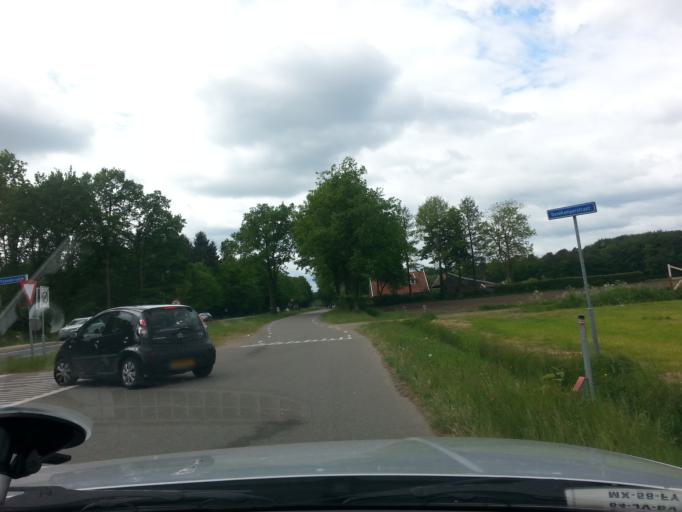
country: NL
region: Overijssel
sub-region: Gemeente Oldenzaal
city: Oldenzaal
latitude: 52.3489
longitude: 6.9731
